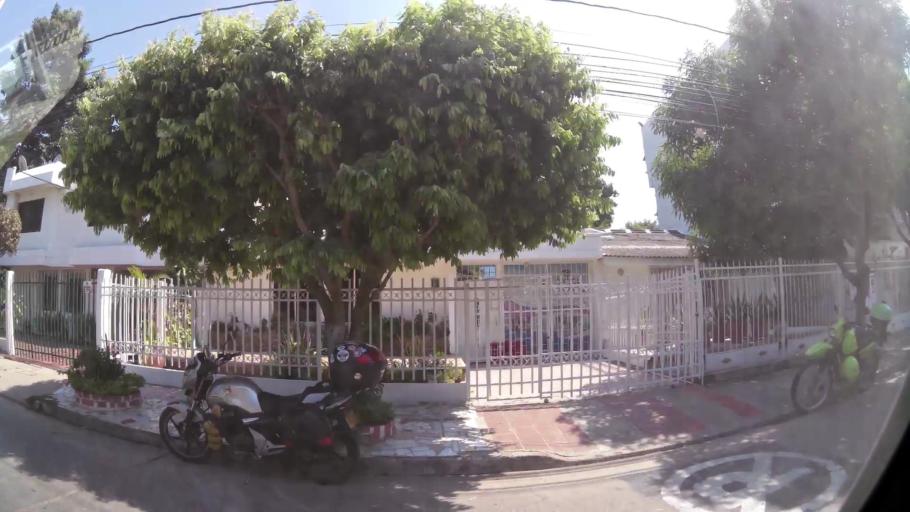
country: CO
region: Bolivar
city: Cartagena
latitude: 10.3932
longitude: -75.4787
